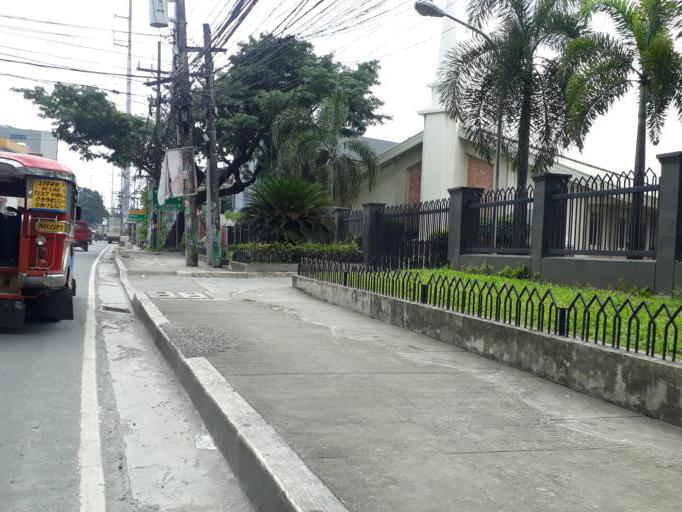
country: PH
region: Calabarzon
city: Bagong Pagasa
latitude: 14.6783
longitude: 121.0292
